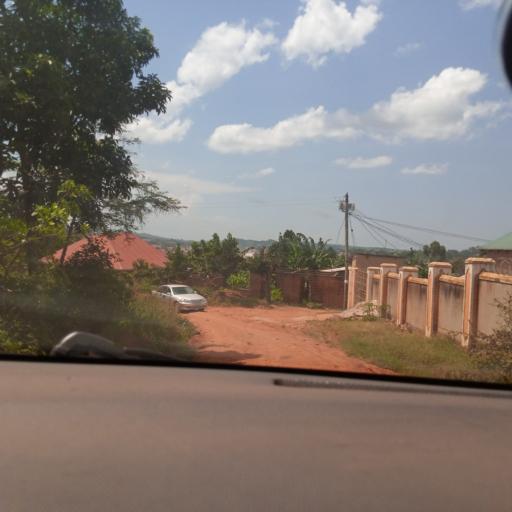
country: UG
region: Central Region
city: Masaka
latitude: -0.3232
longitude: 31.7453
